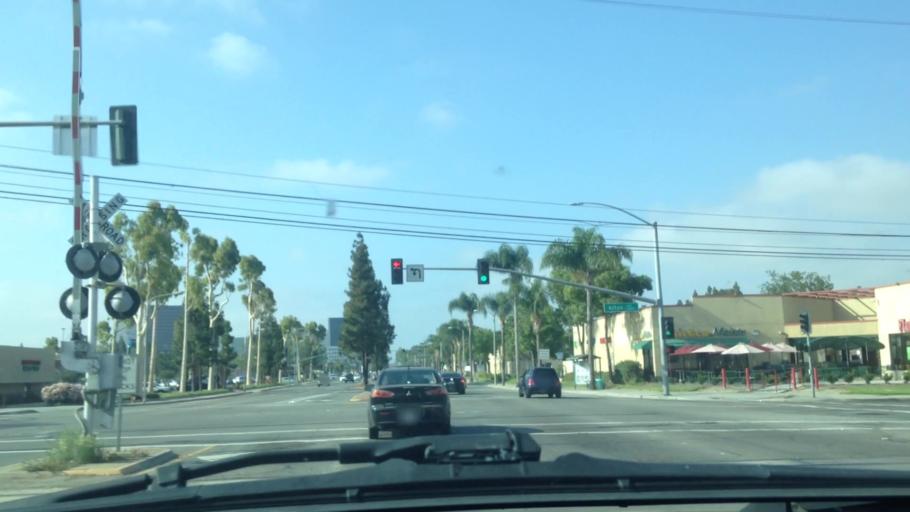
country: US
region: California
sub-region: Orange County
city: Santa Ana
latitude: 33.7040
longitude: -117.8856
